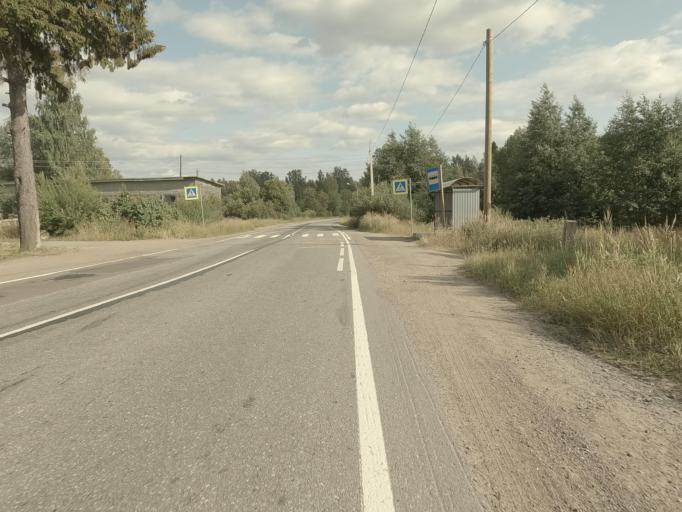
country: RU
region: Leningrad
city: Kamennogorsk
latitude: 60.9409
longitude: 29.1535
